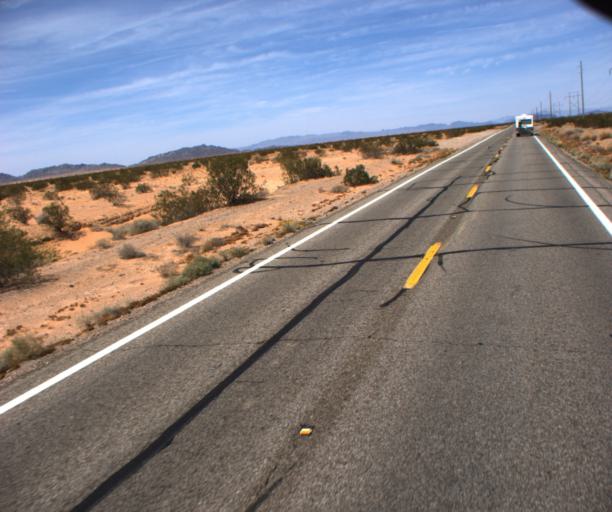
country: US
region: Arizona
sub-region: La Paz County
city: Quartzsite
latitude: 33.8896
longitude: -114.2169
